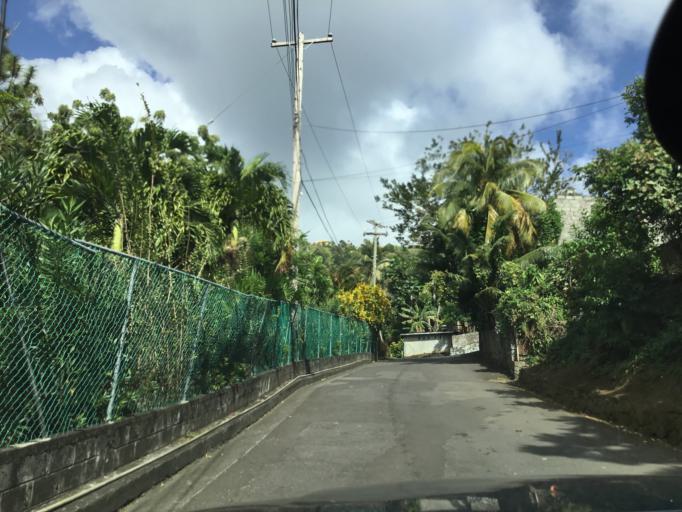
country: VC
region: Saint George
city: Kingstown
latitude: 13.1613
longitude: -61.2185
